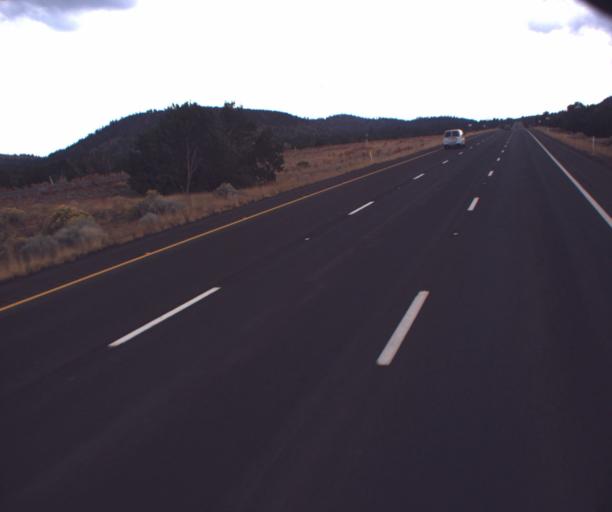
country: US
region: Arizona
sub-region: Coconino County
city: Flagstaff
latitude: 35.4077
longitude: -111.5744
